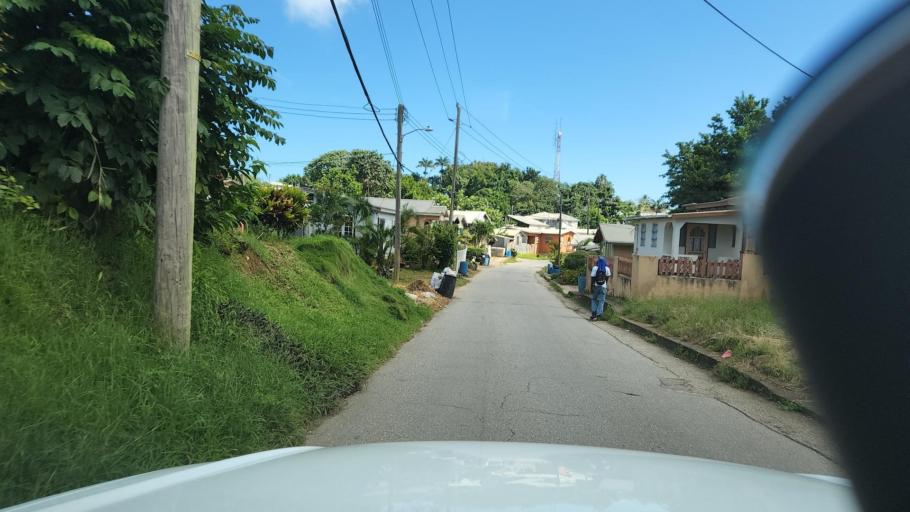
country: BB
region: Saint Thomas
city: Welchman Hall
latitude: 13.1928
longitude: -59.5590
